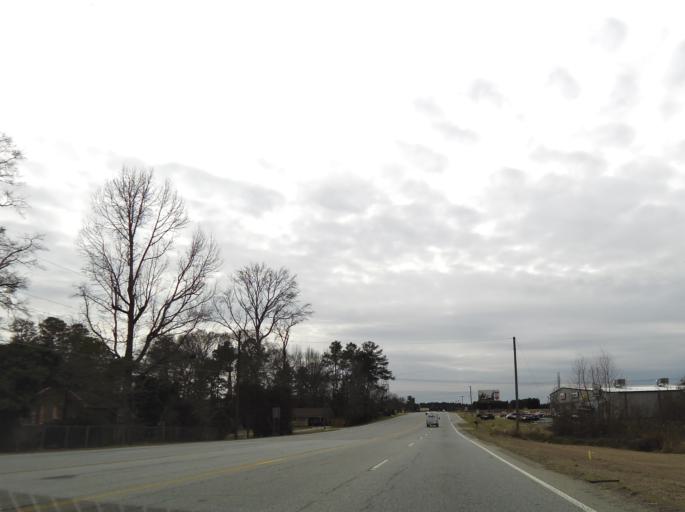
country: US
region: Georgia
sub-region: Peach County
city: Byron
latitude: 32.6437
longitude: -83.7637
